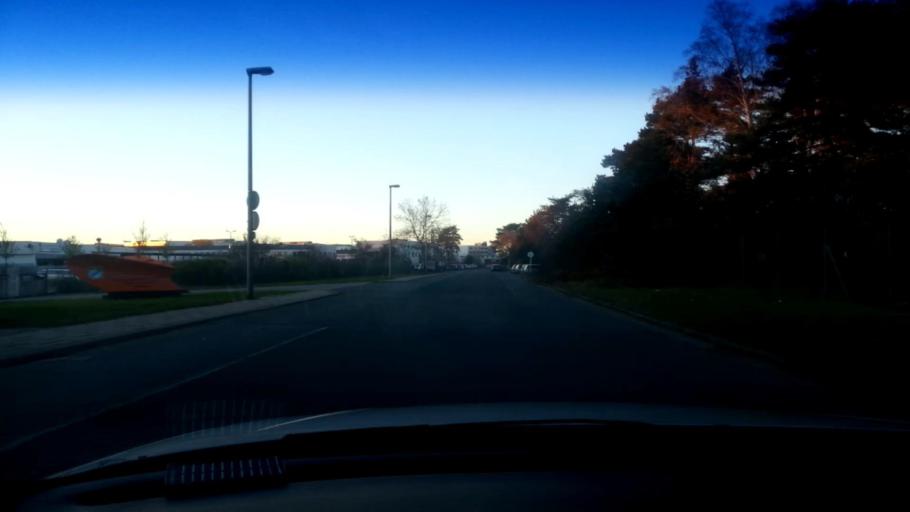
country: DE
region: Bavaria
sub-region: Upper Franconia
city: Bamberg
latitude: 49.8811
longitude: 10.9266
